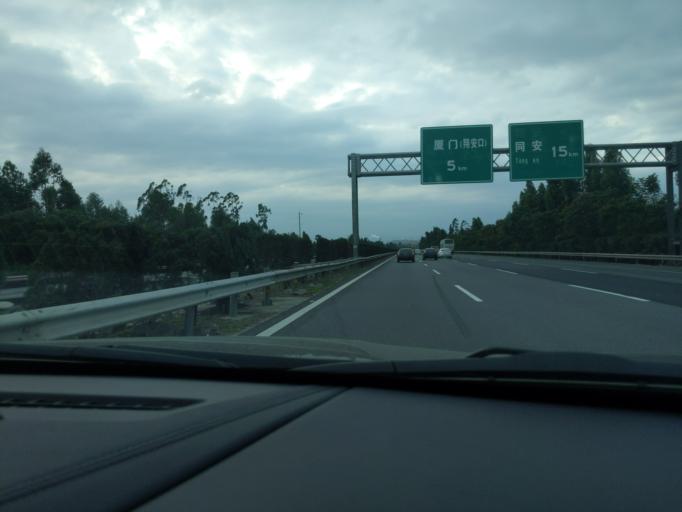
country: CN
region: Fujian
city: Maxiang
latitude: 24.6811
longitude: 118.2767
